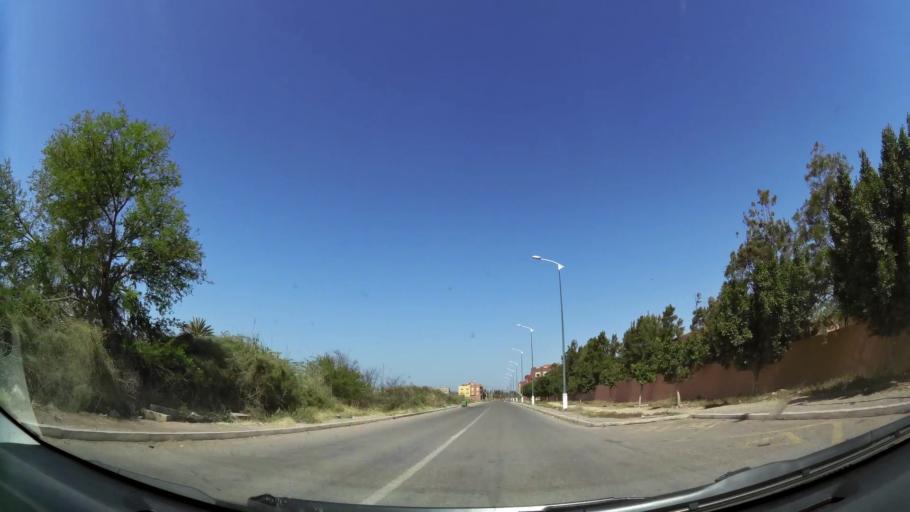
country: MA
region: Souss-Massa-Draa
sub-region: Inezgane-Ait Mellou
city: Inezgane
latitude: 30.3272
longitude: -9.5077
